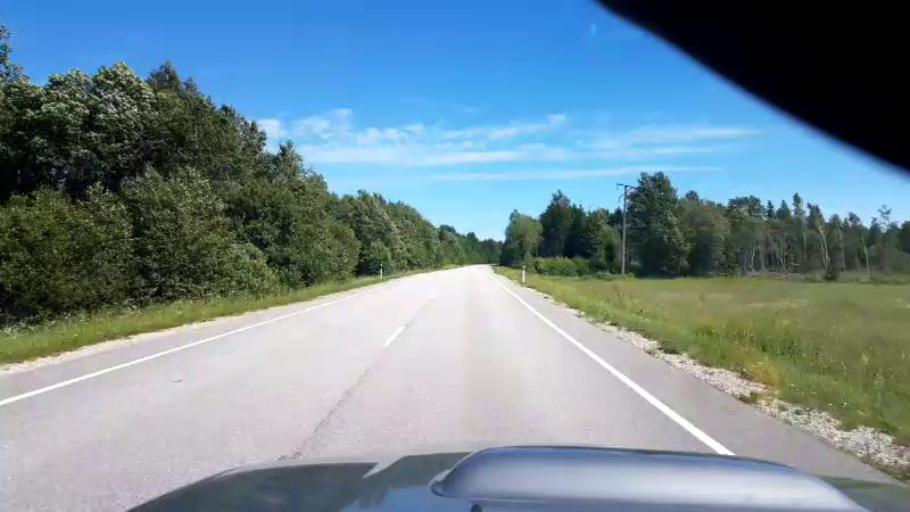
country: EE
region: Jaervamaa
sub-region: Koeru vald
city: Koeru
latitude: 58.9767
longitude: 26.1062
